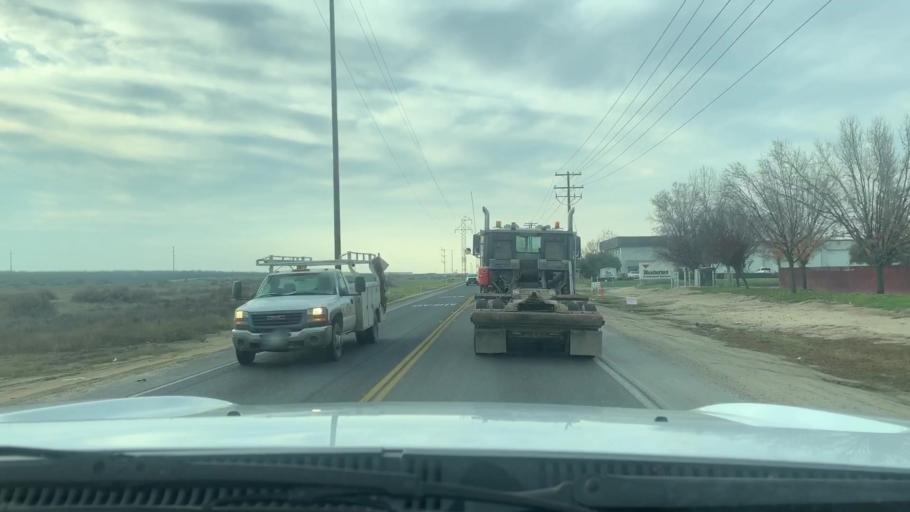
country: US
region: California
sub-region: Kern County
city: Shafter
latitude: 35.4417
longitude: -119.2535
